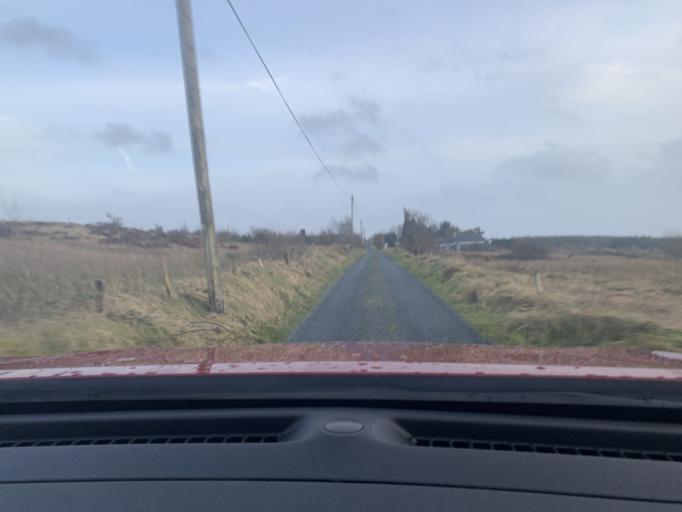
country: IE
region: Connaught
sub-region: Roscommon
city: Ballaghaderreen
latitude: 53.9551
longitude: -8.5294
